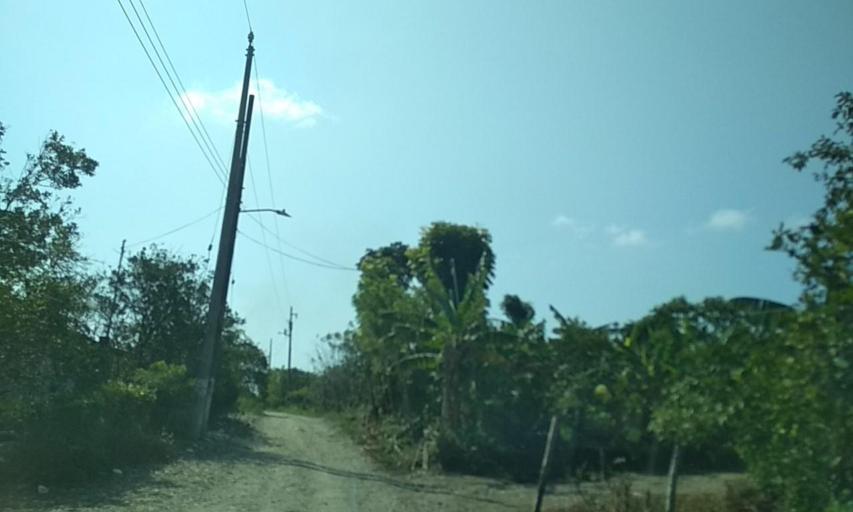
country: MX
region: Veracruz
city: Gutierrez Zamora
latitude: 20.3757
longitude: -97.1485
